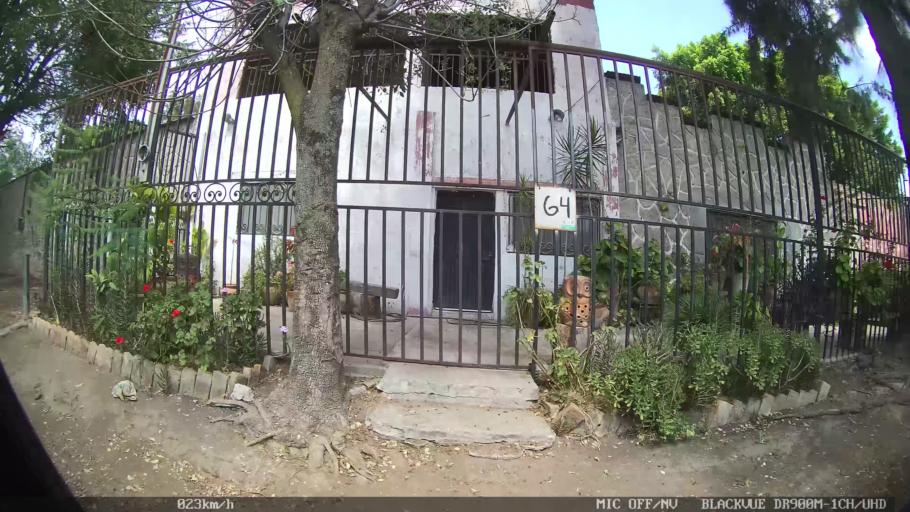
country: MX
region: Jalisco
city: Tonala
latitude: 20.6238
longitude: -103.2653
